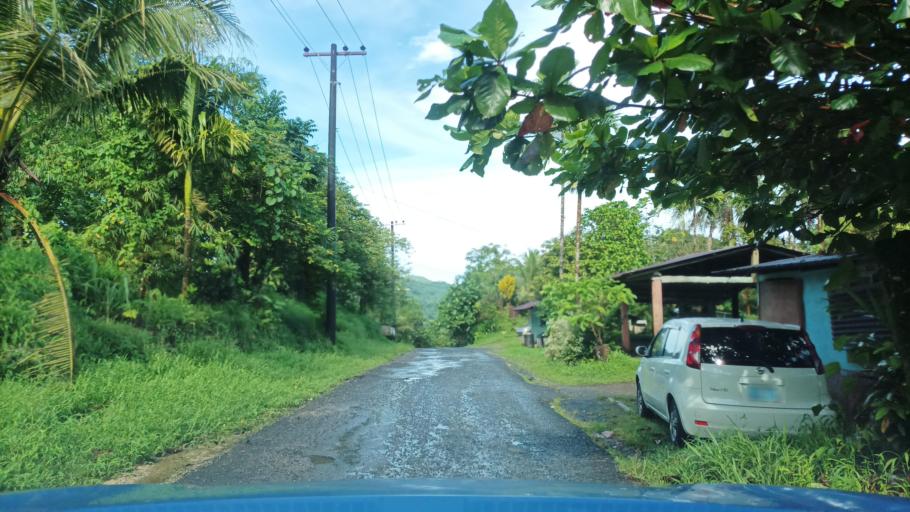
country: FM
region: Pohnpei
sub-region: Sokehs Municipality
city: Palikir - National Government Center
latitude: 6.9331
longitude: 158.1900
